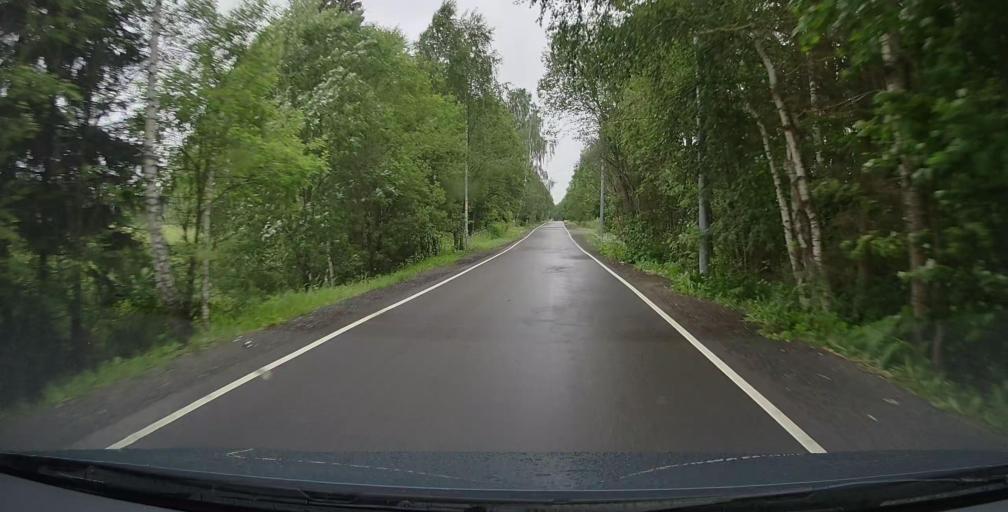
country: RU
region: Moskovskaya
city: Selyatino
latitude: 55.4006
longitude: 37.0172
